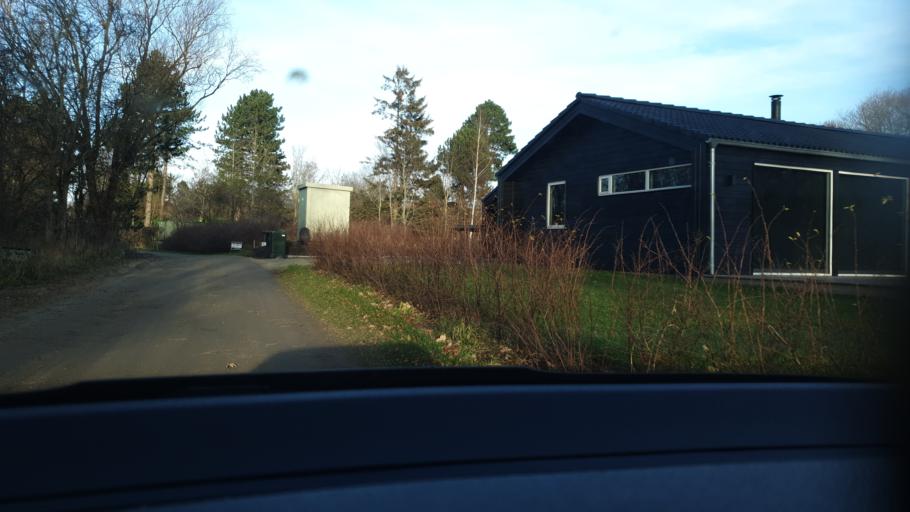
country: DK
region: Zealand
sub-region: Odsherred Kommune
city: Hojby
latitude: 55.9323
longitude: 11.6232
